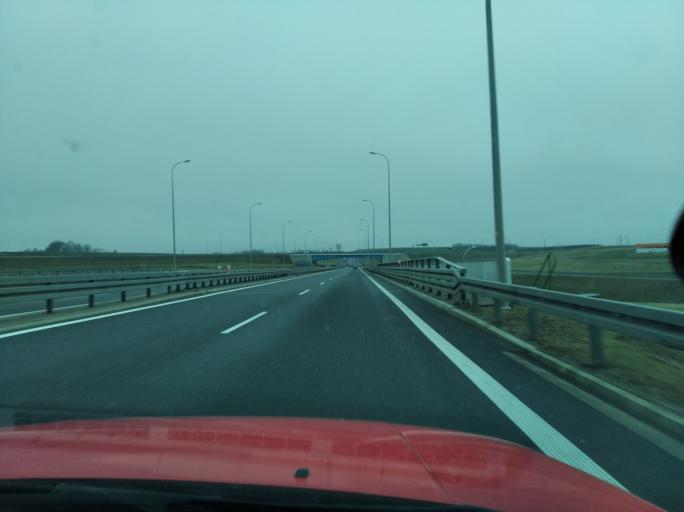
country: PL
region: Subcarpathian Voivodeship
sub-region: Powiat przeworski
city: Mirocin
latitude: 50.0373
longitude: 22.5777
